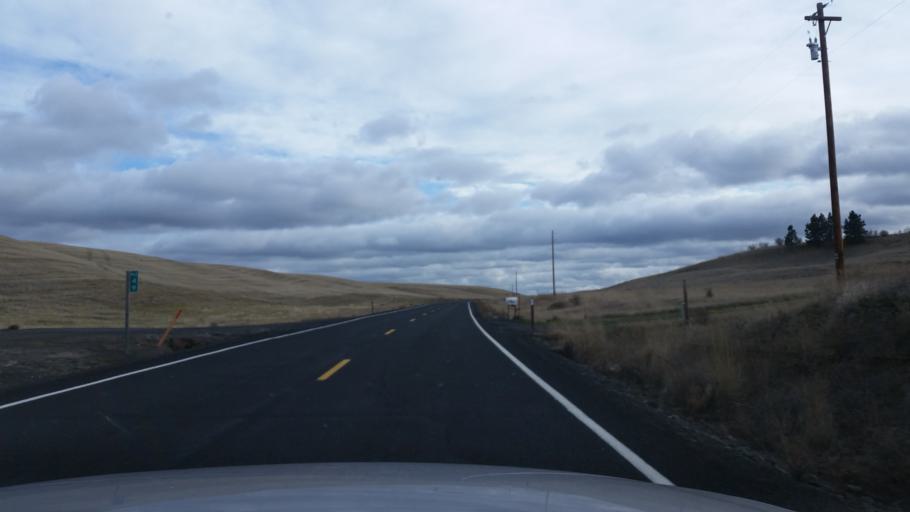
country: US
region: Washington
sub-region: Lincoln County
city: Davenport
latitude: 47.3574
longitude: -118.0390
